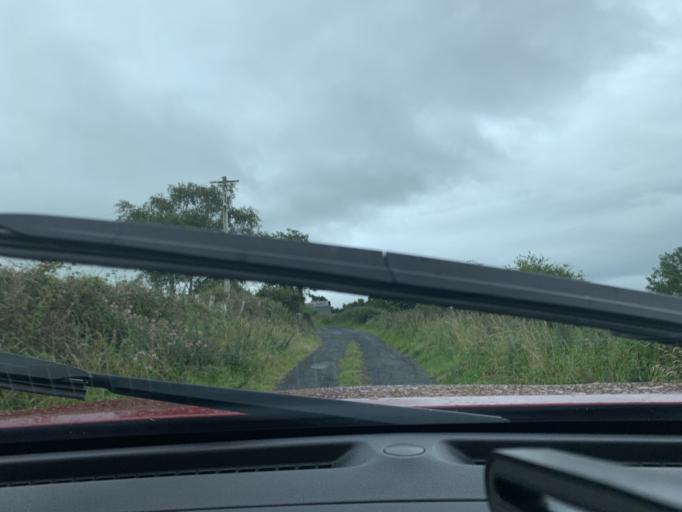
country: IE
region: Connaught
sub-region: Sligo
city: Sligo
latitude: 54.3049
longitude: -8.4483
